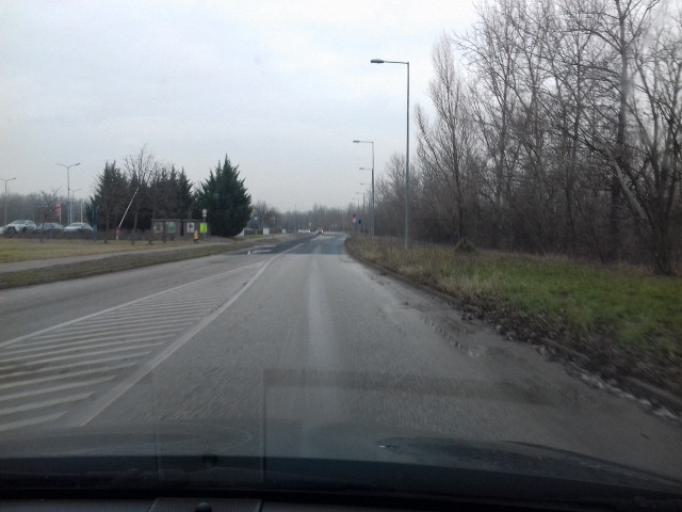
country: HU
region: Budapest
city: Budapest XV. keruelet
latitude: 47.5990
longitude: 19.1120
